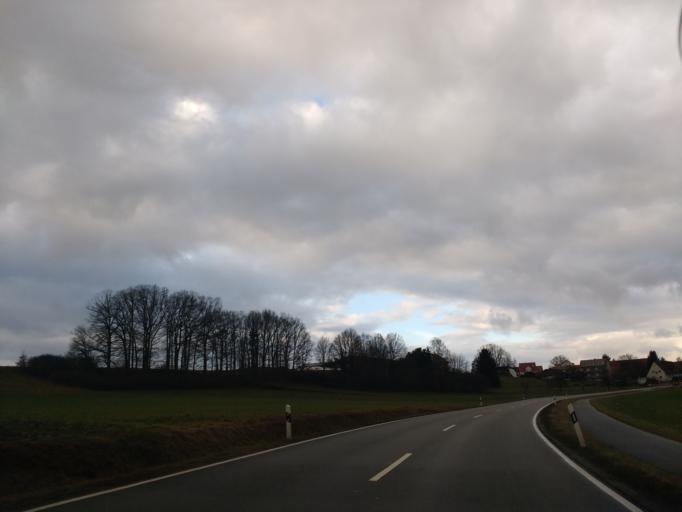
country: DE
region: Bavaria
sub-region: Regierungsbezirk Mittelfranken
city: Herzogenaurach
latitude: 49.5800
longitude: 10.8610
